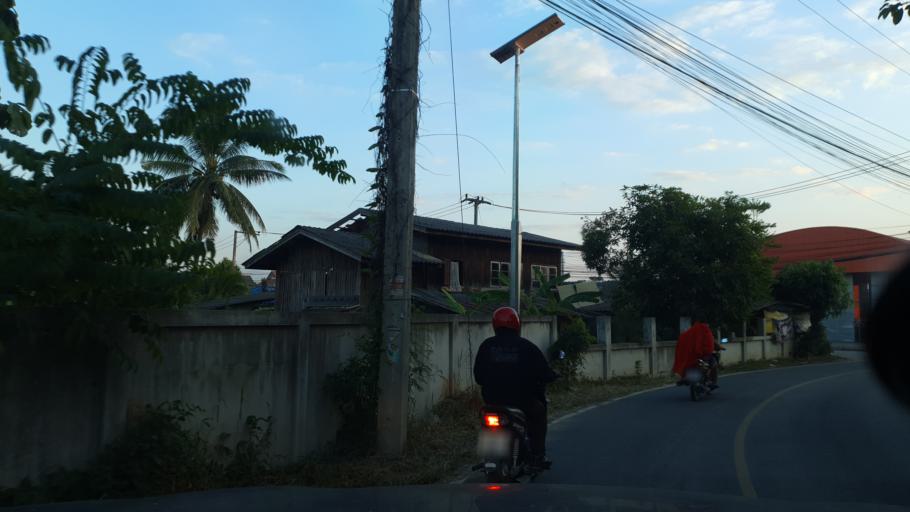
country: TH
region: Chiang Mai
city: San Sai
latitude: 18.8530
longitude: 99.0732
